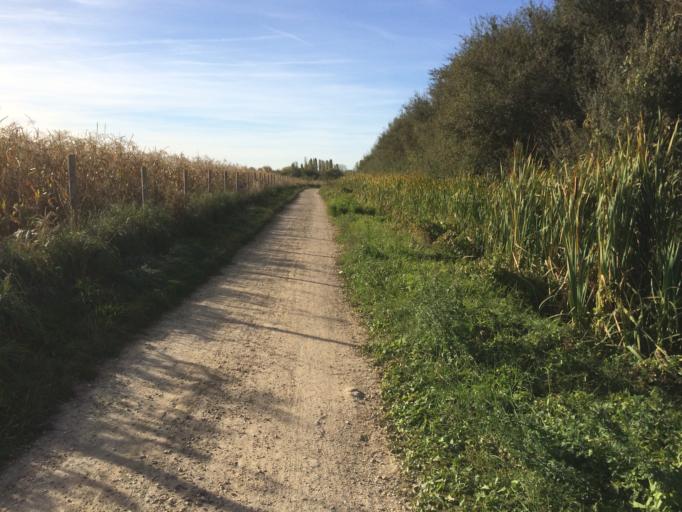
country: FR
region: Ile-de-France
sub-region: Departement de l'Essonne
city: Vauhallan
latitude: 48.7295
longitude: 2.1901
